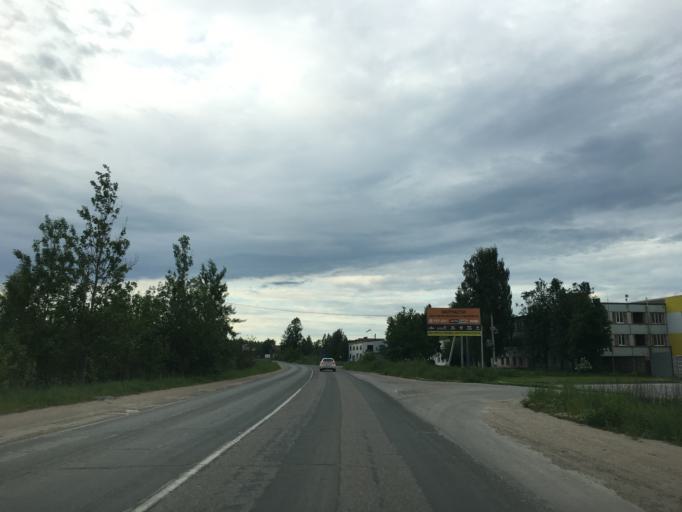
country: RU
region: Pskov
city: Pskov
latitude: 57.8502
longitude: 28.3079
